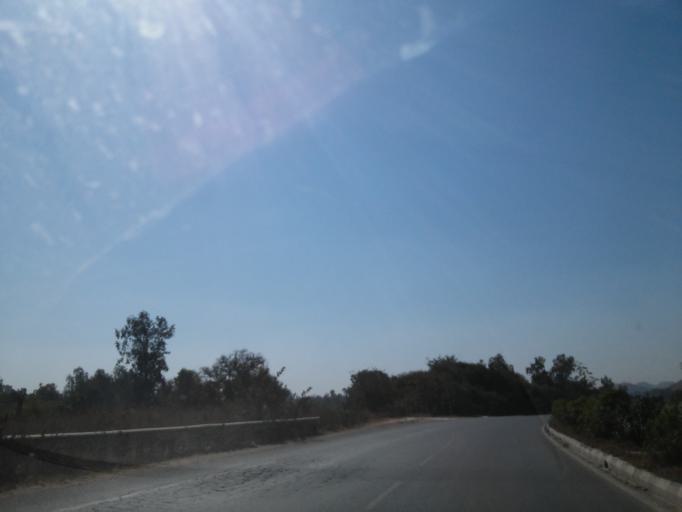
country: IN
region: Rajasthan
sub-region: Dungarpur
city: Dungarpur
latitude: 23.8232
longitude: 73.5208
